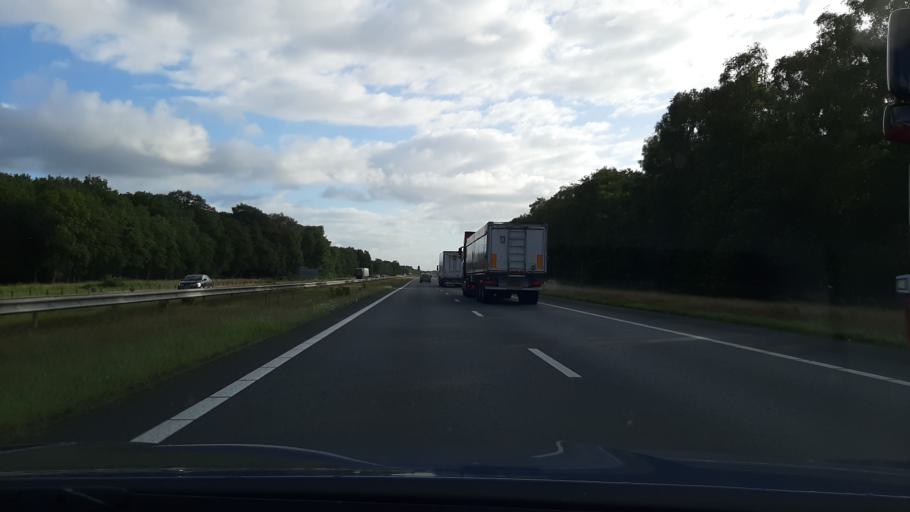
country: NL
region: Friesland
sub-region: Gemeente Smallingerland
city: Boornbergum
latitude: 53.0685
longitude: 6.0586
